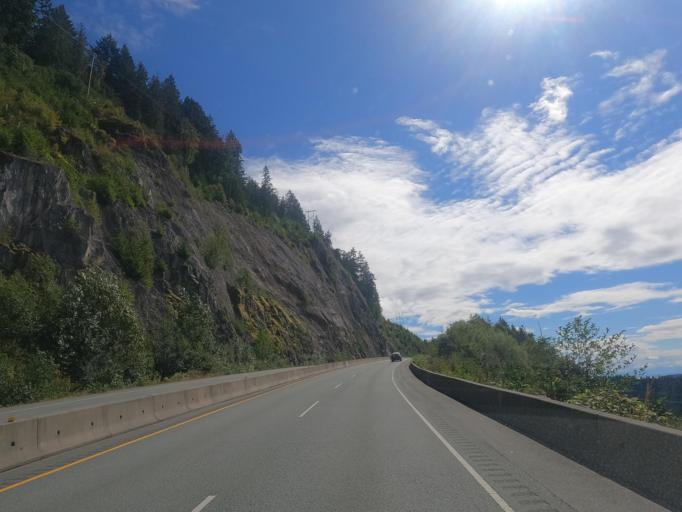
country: CA
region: British Columbia
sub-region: Greater Vancouver Regional District
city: Lions Bay
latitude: 49.3836
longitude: -123.2612
